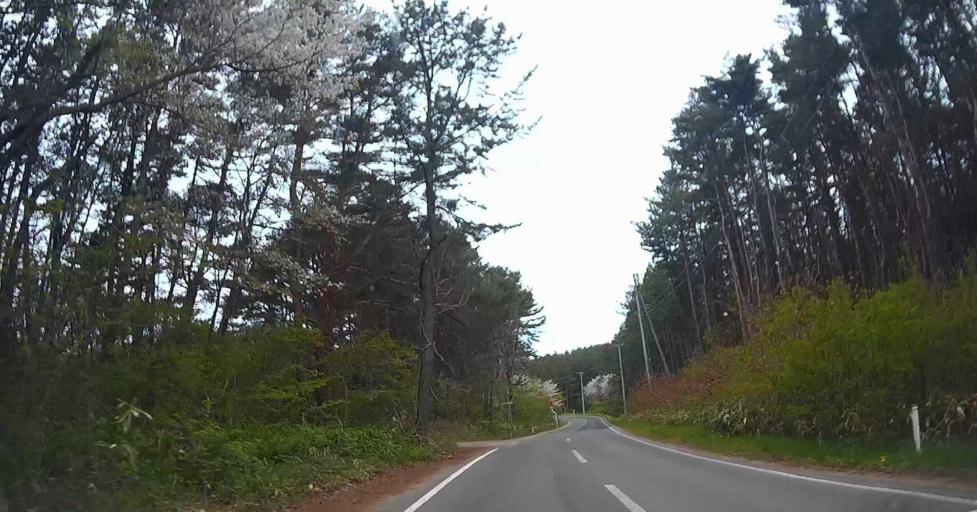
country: JP
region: Aomori
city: Shimokizukuri
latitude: 40.9371
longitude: 140.3354
